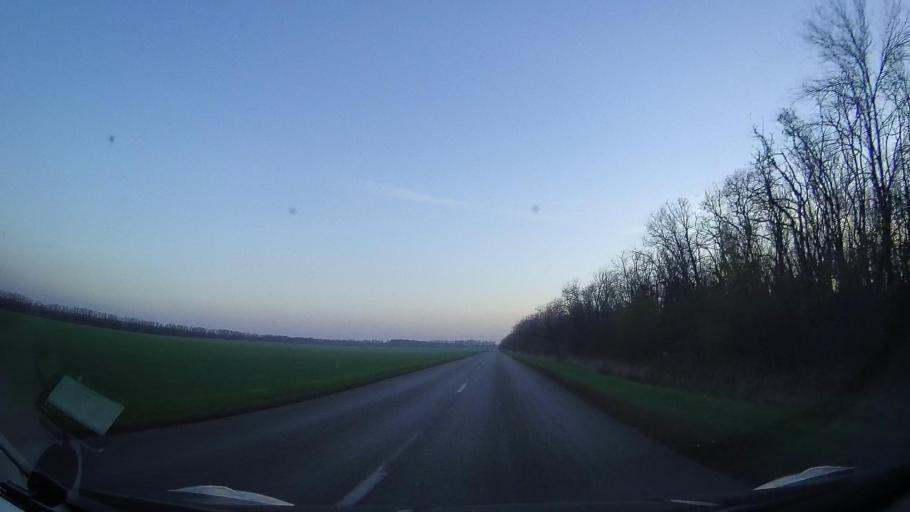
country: RU
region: Rostov
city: Zernograd
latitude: 46.9768
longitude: 40.3915
